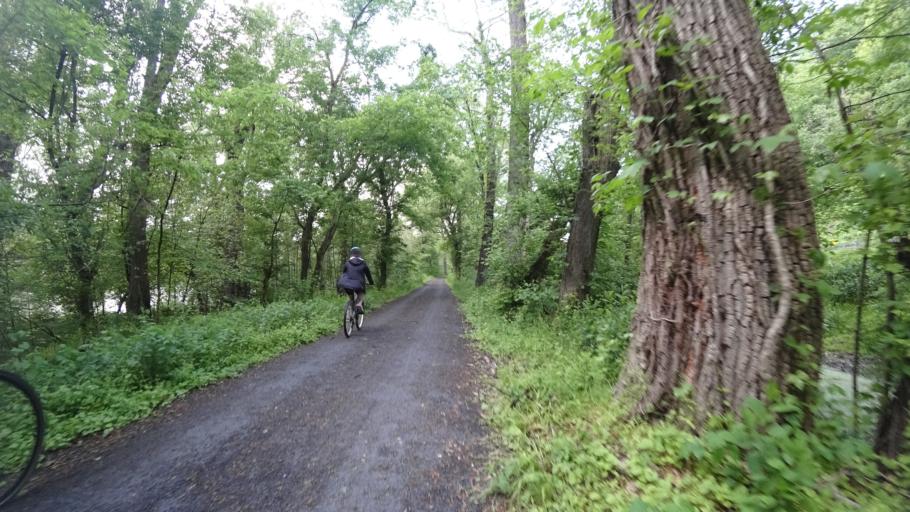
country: US
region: Maryland
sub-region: Frederick County
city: Point of Rocks
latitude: 39.2921
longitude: -77.5568
